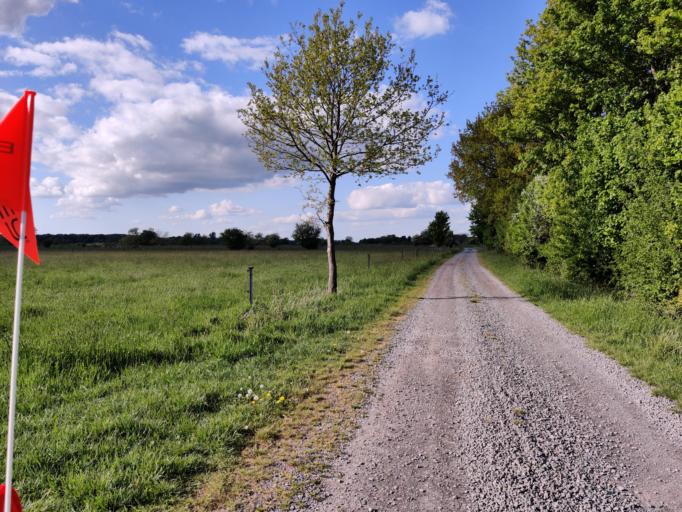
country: DE
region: Lower Saxony
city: Wunstorf
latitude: 52.4504
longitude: 9.4737
